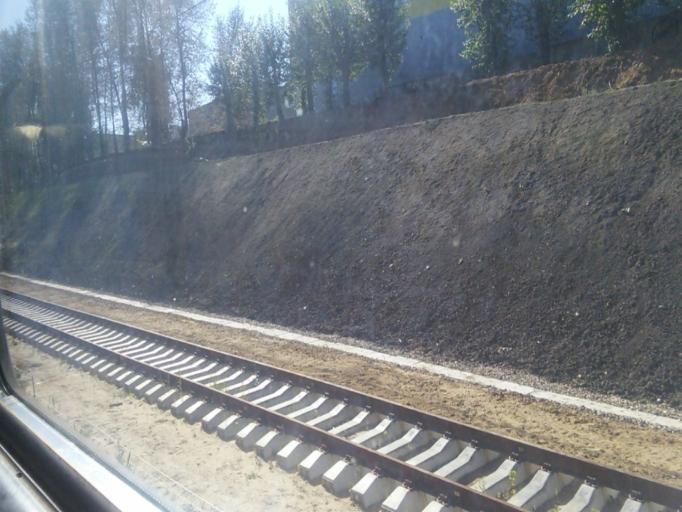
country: RU
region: Moskovskaya
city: Saltykovka
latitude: 55.7543
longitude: 37.9425
